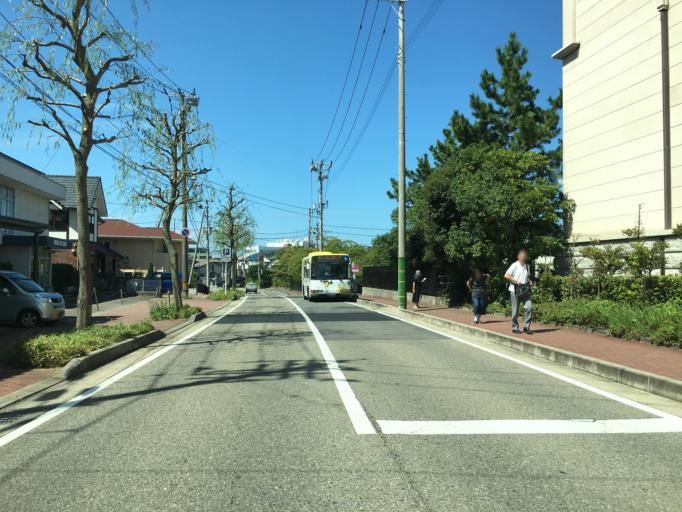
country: JP
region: Niigata
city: Niigata-shi
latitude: 37.9296
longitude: 139.0576
